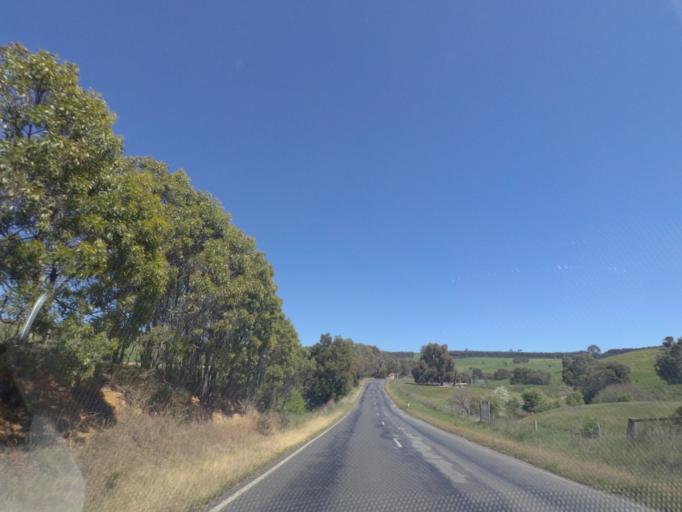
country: AU
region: Victoria
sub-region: Whittlesea
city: Whittlesea
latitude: -37.2657
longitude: 145.0331
